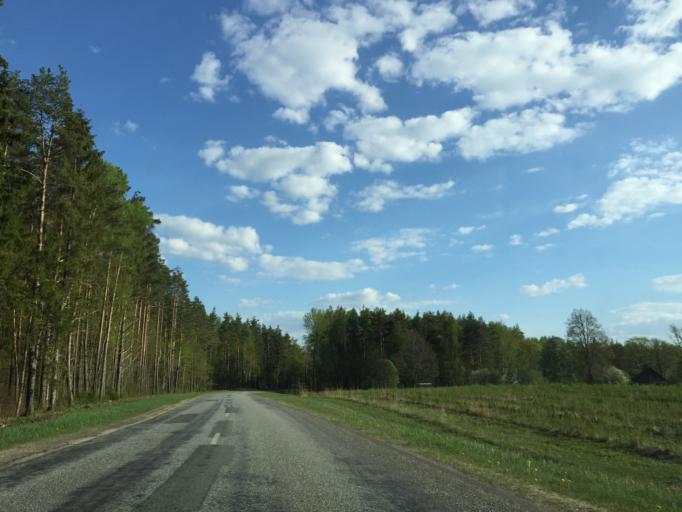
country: LV
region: Sigulda
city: Sigulda
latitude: 57.2177
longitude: 24.8561
